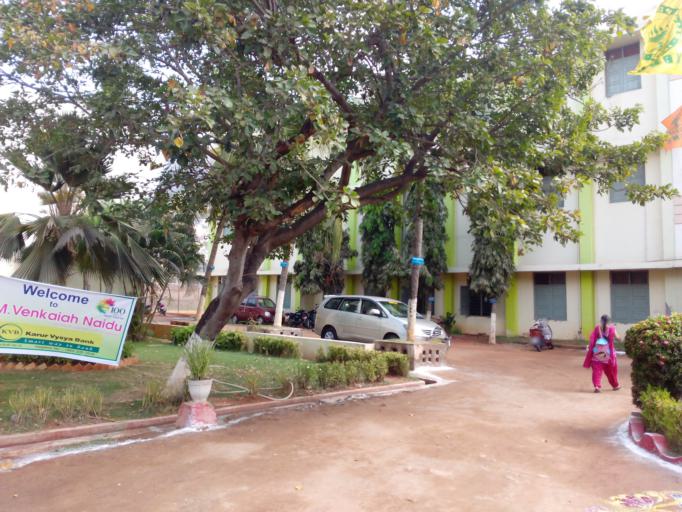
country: IN
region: Andhra Pradesh
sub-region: Krishna
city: Vijayawada
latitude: 16.5230
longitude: 80.6123
